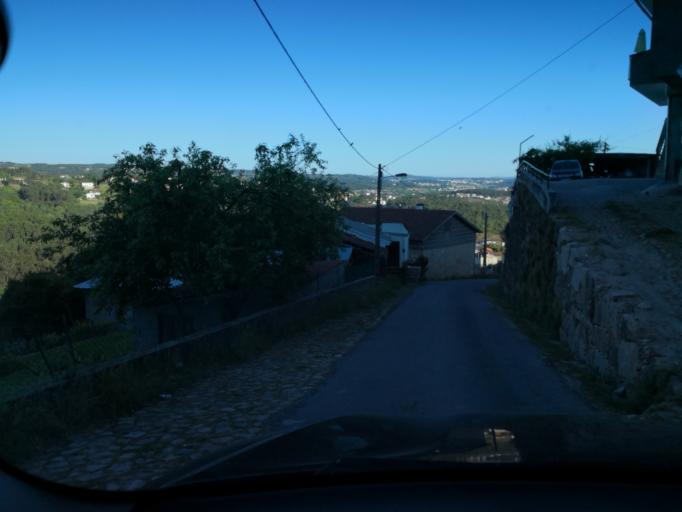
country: PT
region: Vila Real
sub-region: Vila Real
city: Vila Real
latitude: 41.3427
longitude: -7.7382
